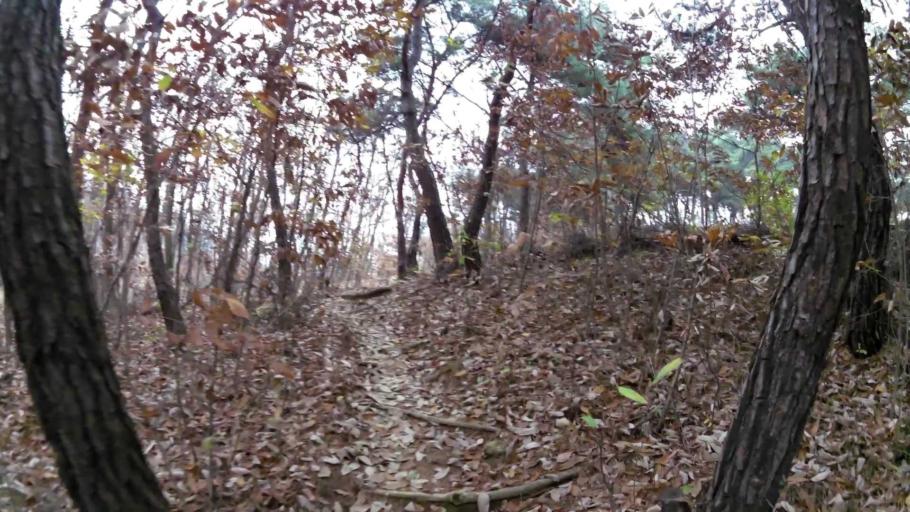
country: KR
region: Daegu
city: Daegu
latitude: 35.8608
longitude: 128.6620
